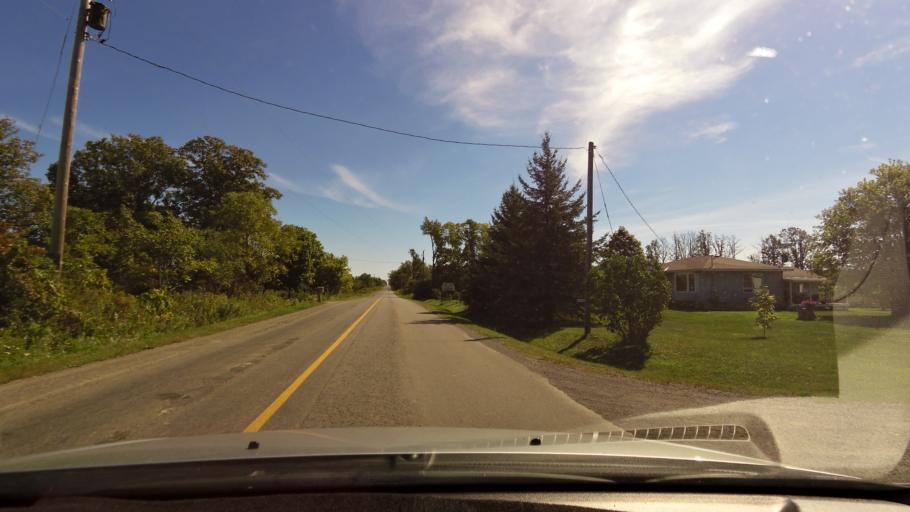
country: CA
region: Ontario
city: Ancaster
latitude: 43.0725
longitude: -80.0722
